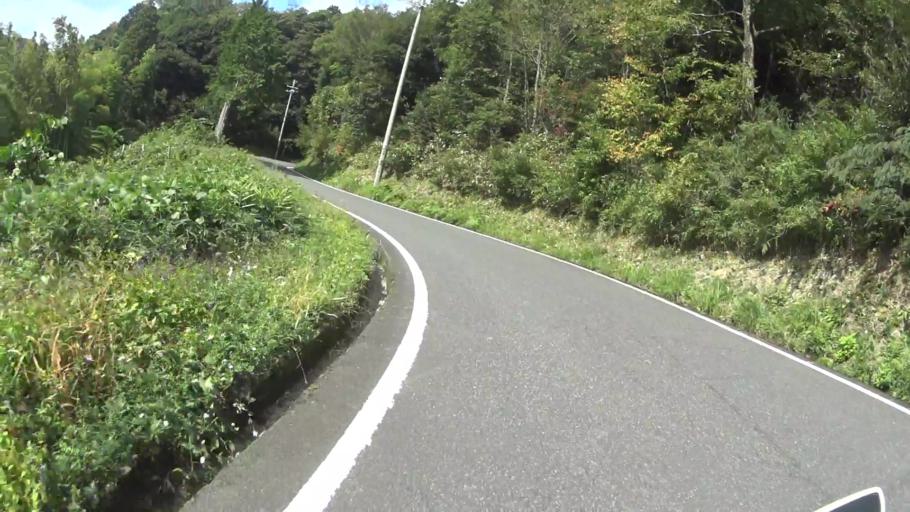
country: JP
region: Kyoto
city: Miyazu
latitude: 35.6802
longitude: 135.2677
